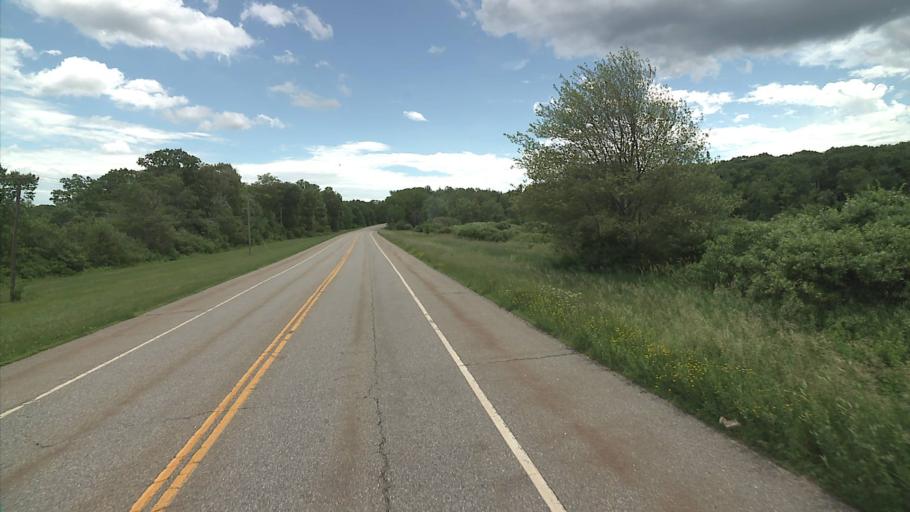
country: US
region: Connecticut
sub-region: Litchfield County
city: Litchfield
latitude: 41.7797
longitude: -73.2052
